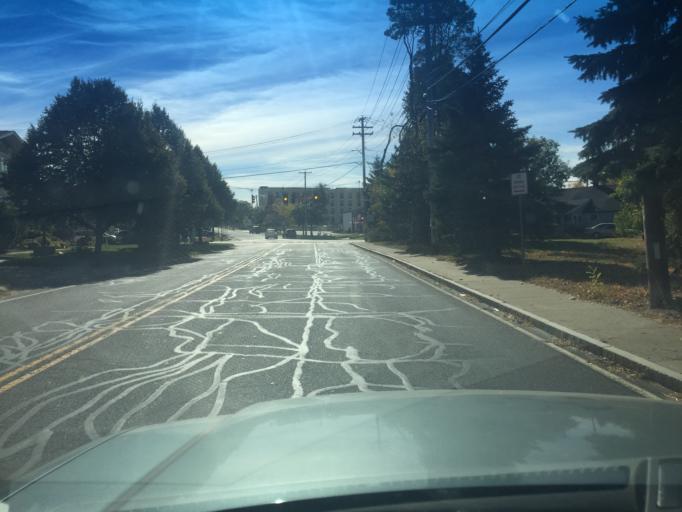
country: US
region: Massachusetts
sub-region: Norfolk County
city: Franklin
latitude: 42.0676
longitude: -71.3994
